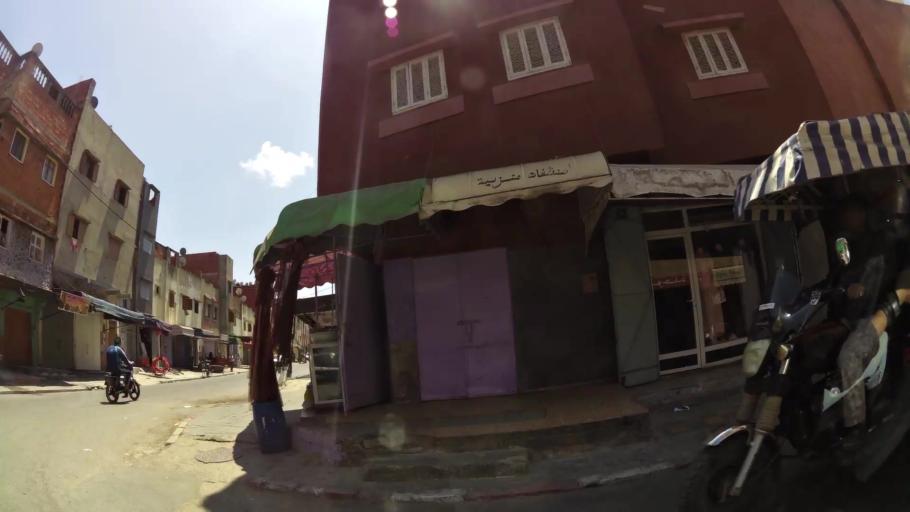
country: MA
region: Gharb-Chrarda-Beni Hssen
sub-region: Kenitra Province
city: Kenitra
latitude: 34.2530
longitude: -6.5502
